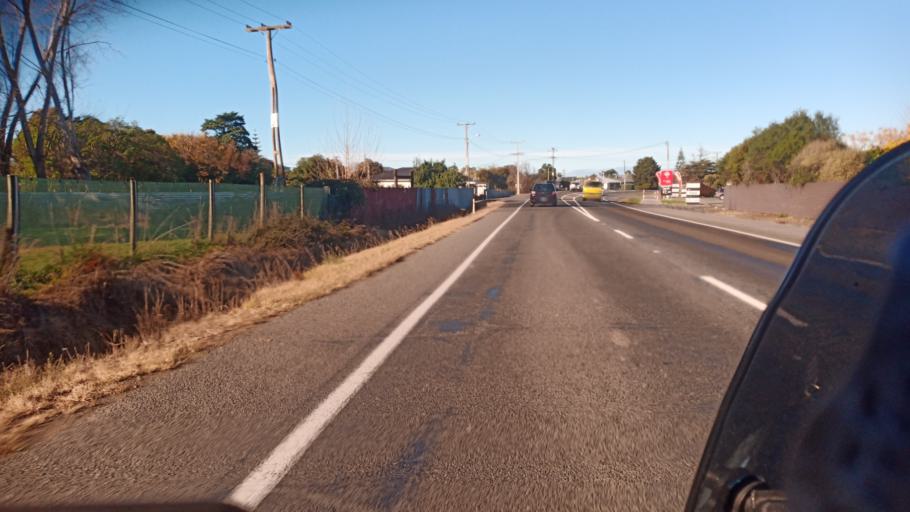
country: NZ
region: Hawke's Bay
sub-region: Napier City
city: Napier
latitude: -39.4279
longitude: 176.8715
